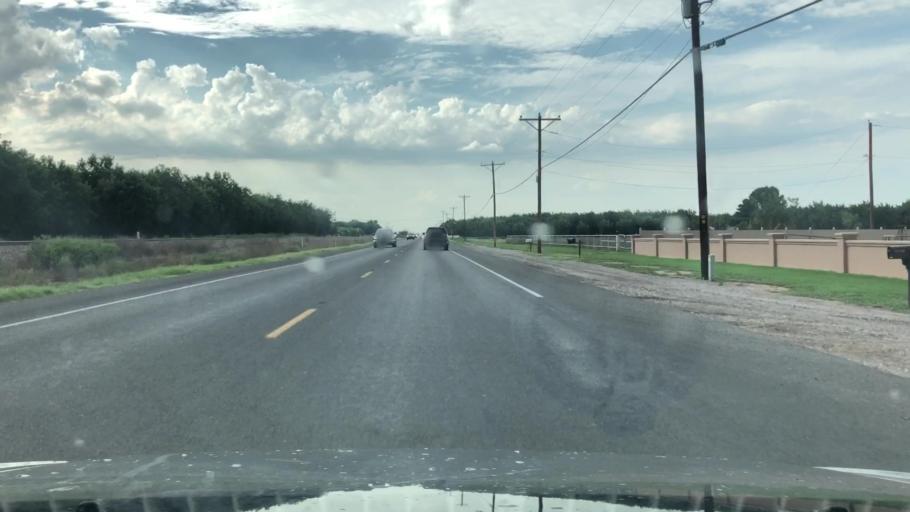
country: US
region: New Mexico
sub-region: Dona Ana County
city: San Miguel
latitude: 32.2177
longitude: -106.7300
